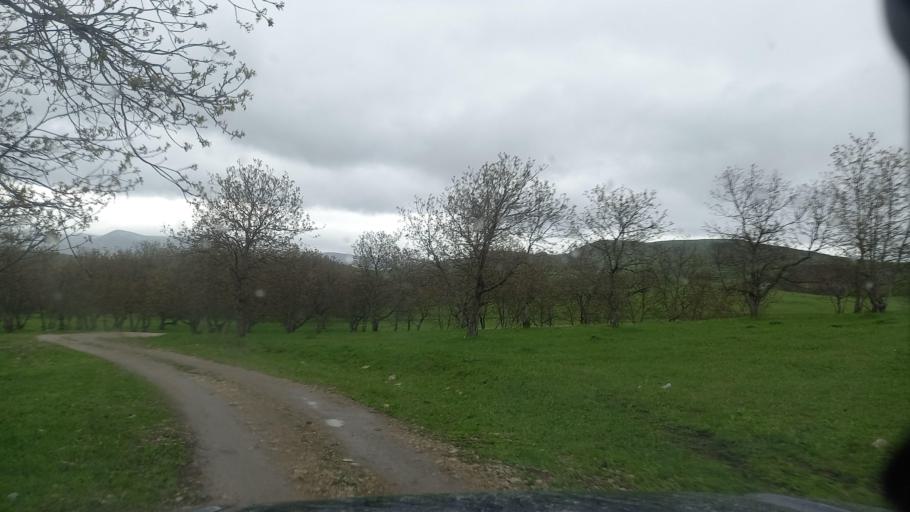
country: RU
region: Kabardino-Balkariya
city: Kamennomostskoye
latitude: 43.7063
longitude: 43.0705
